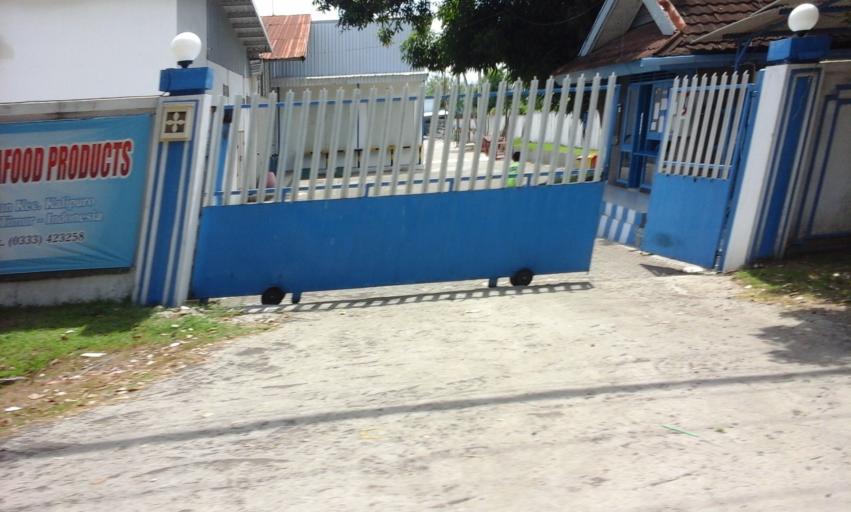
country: ID
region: East Java
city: Klatakan
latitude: -8.1677
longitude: 114.3878
